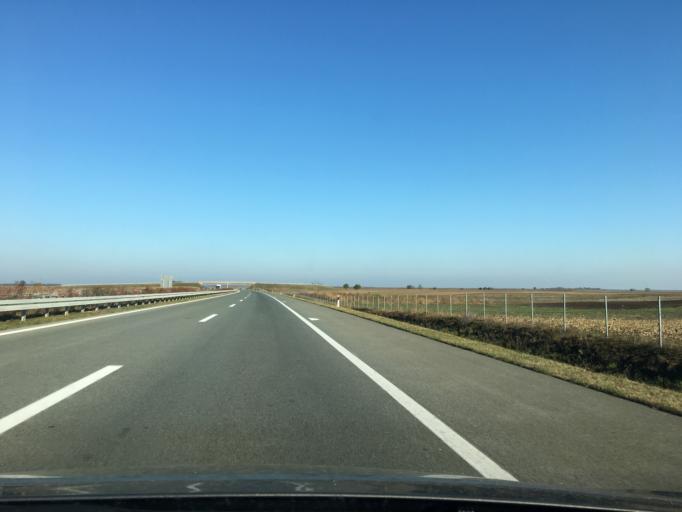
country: RS
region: Autonomna Pokrajina Vojvodina
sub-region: Severnobacki Okrug
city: Mali Igos
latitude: 45.6607
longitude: 19.7261
